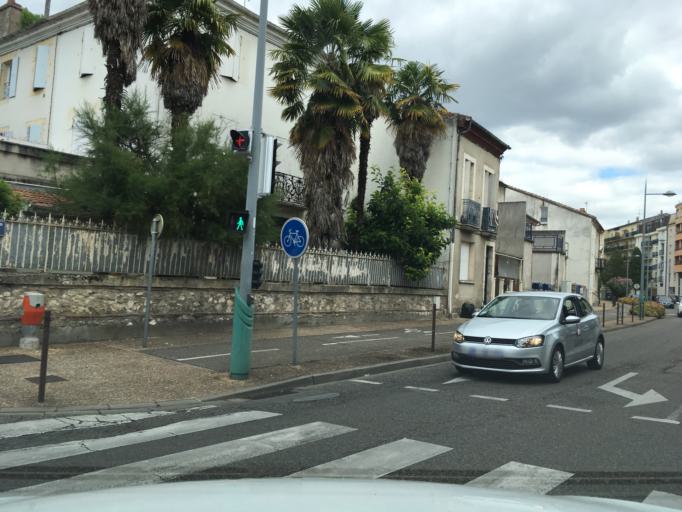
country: FR
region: Aquitaine
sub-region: Departement du Lot-et-Garonne
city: Le Passage
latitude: 44.1954
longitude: 0.6170
